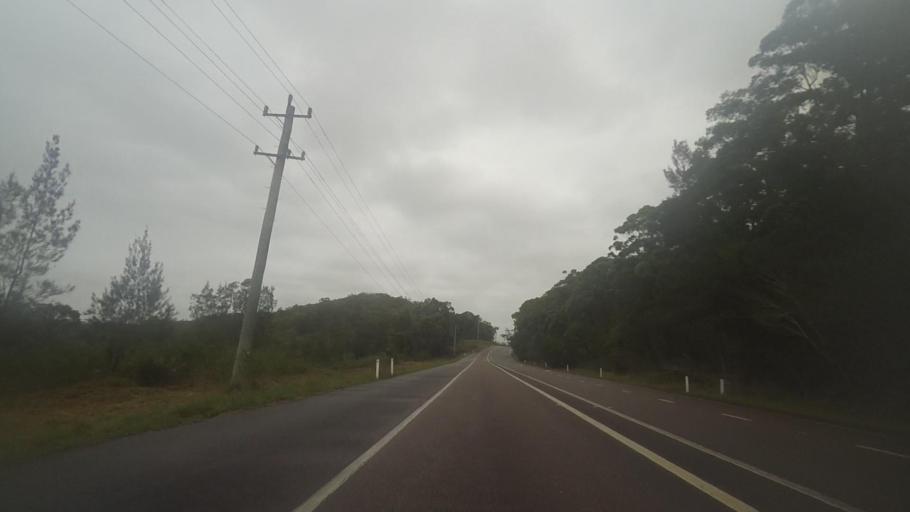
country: AU
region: New South Wales
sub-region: Port Stephens Shire
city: Port Stephens
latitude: -32.6425
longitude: 151.9876
